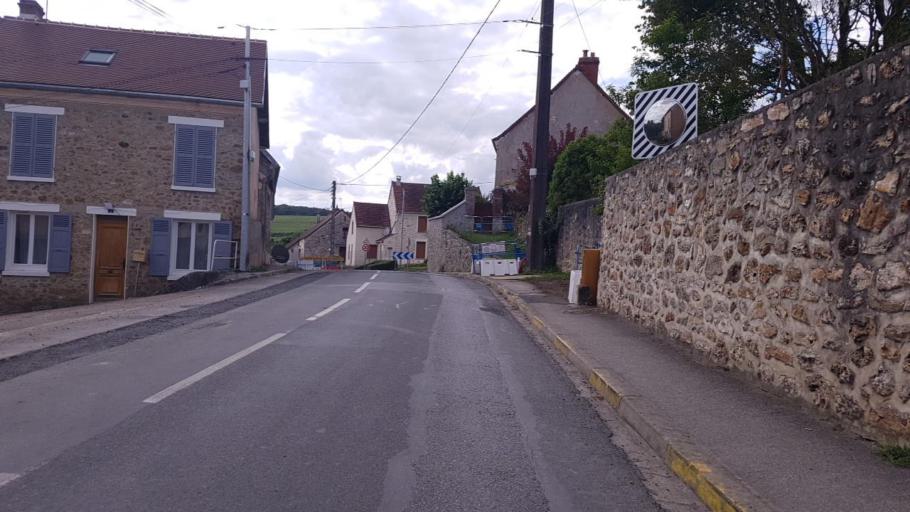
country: FR
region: Picardie
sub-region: Departement de l'Aisne
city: Crezancy
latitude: 49.0758
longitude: 3.5022
